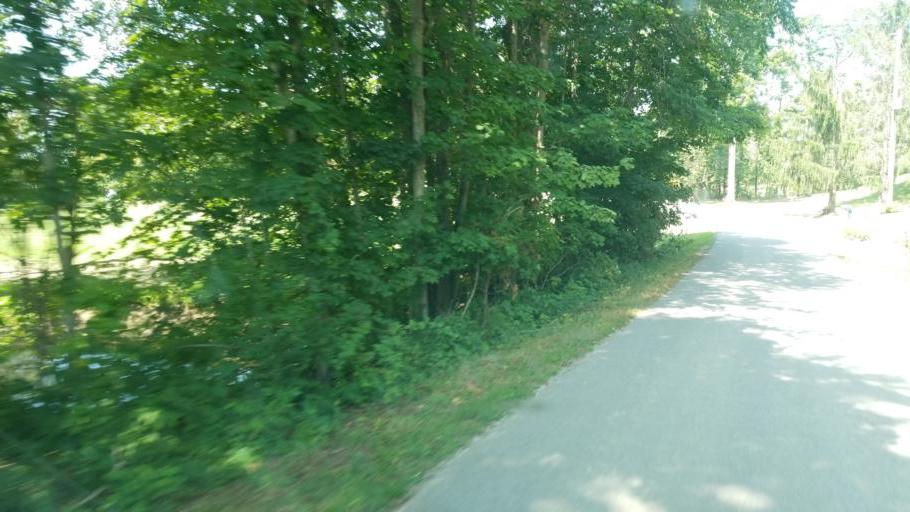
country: US
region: Ohio
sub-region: Crawford County
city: Bucyrus
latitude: 40.7983
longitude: -83.1112
